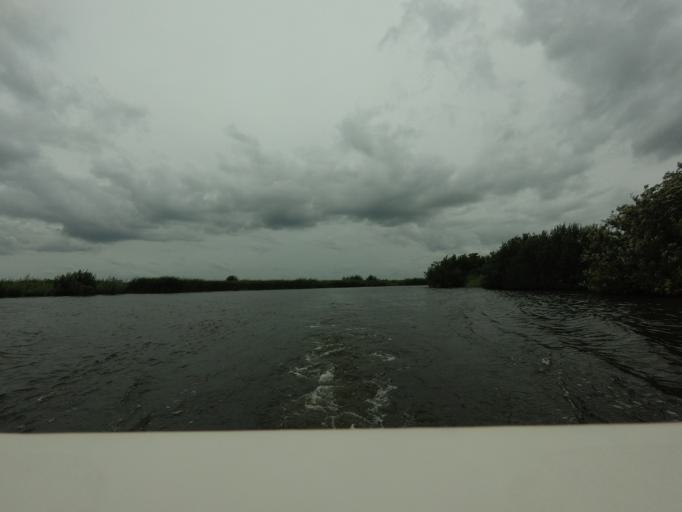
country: NL
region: Friesland
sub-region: Gemeente Boarnsterhim
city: Aldeboarn
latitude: 53.0969
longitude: 5.9195
